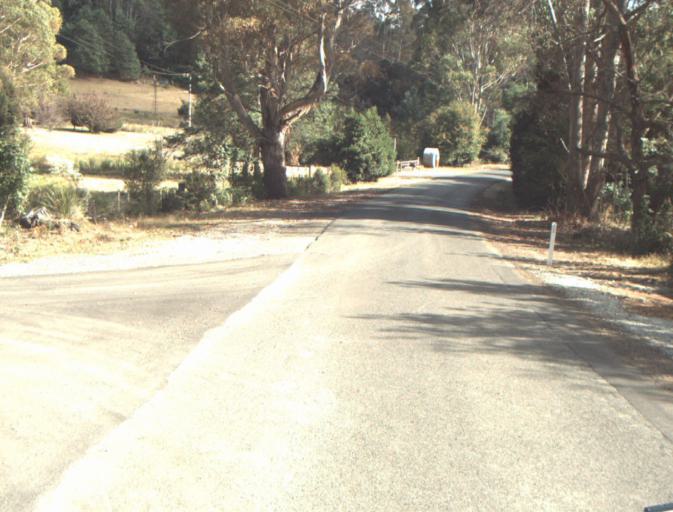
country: AU
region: Tasmania
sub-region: Launceston
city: Mayfield
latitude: -41.3046
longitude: 147.1982
